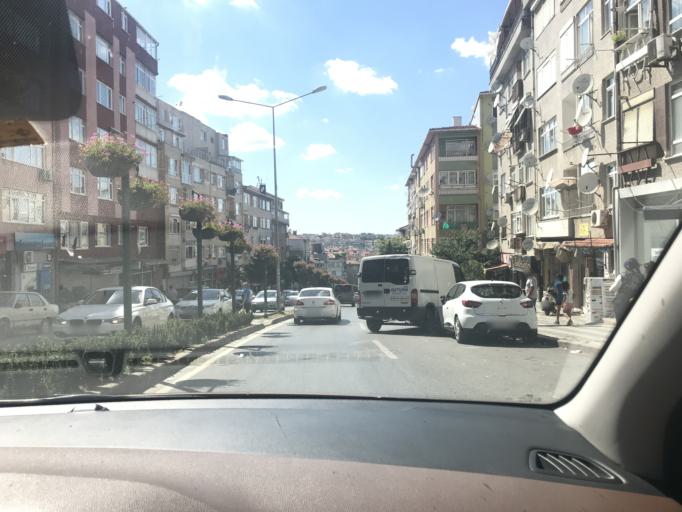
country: TR
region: Istanbul
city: UEskuedar
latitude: 41.0171
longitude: 29.0234
